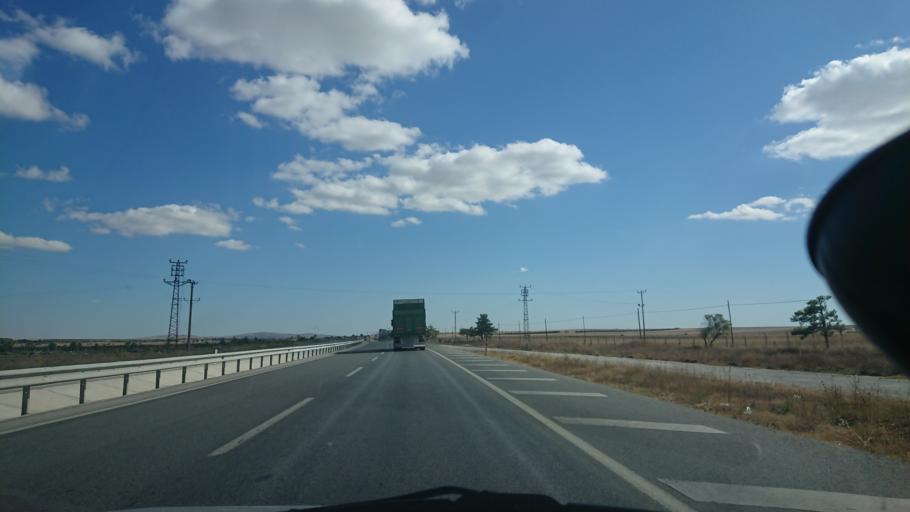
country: TR
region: Eskisehir
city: Mahmudiye
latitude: 39.5591
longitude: 30.9178
